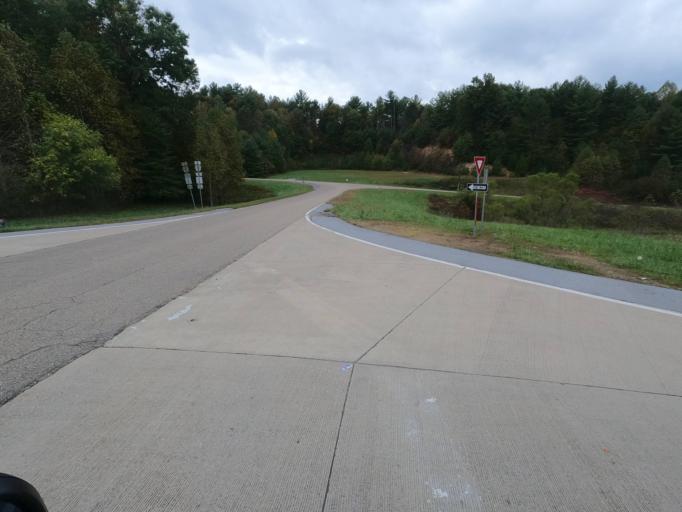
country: US
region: Tennessee
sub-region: Unicoi County
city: Banner Hill
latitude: 36.0520
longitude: -82.5145
